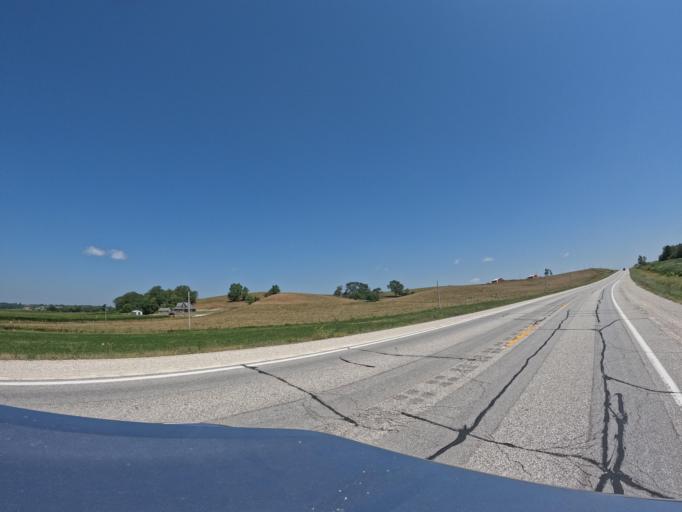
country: US
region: Iowa
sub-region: Keokuk County
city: Sigourney
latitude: 41.2425
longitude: -92.2126
